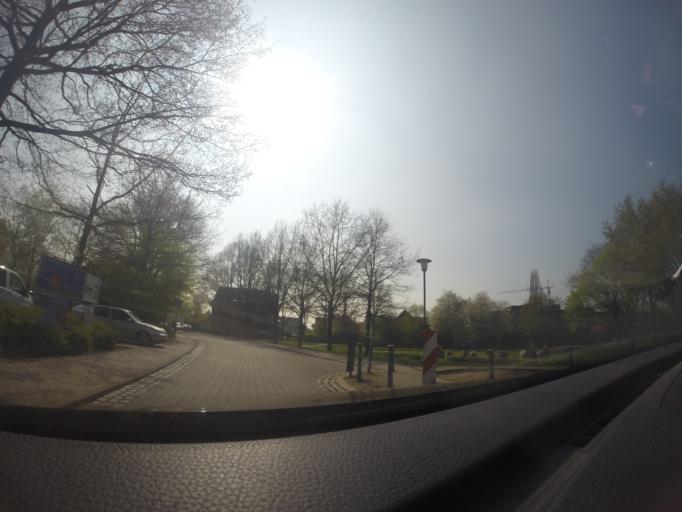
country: DE
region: North Rhine-Westphalia
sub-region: Regierungsbezirk Dusseldorf
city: Xanten
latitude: 51.6590
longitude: 6.4547
